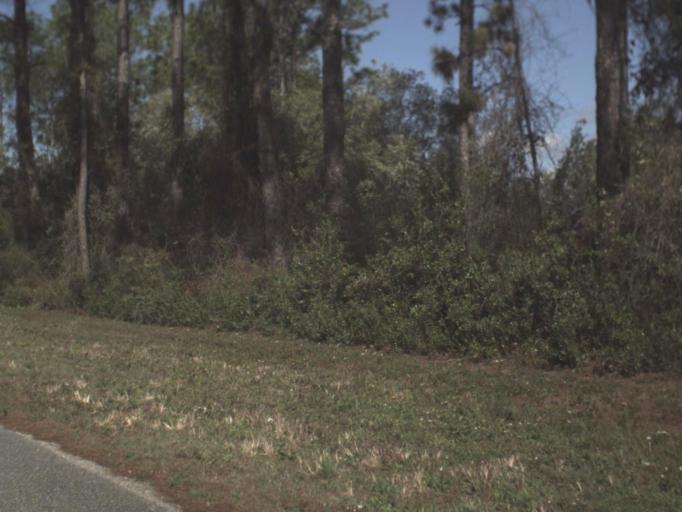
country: US
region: Florida
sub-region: Gulf County
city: Port Saint Joe
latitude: 29.7431
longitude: -85.2305
